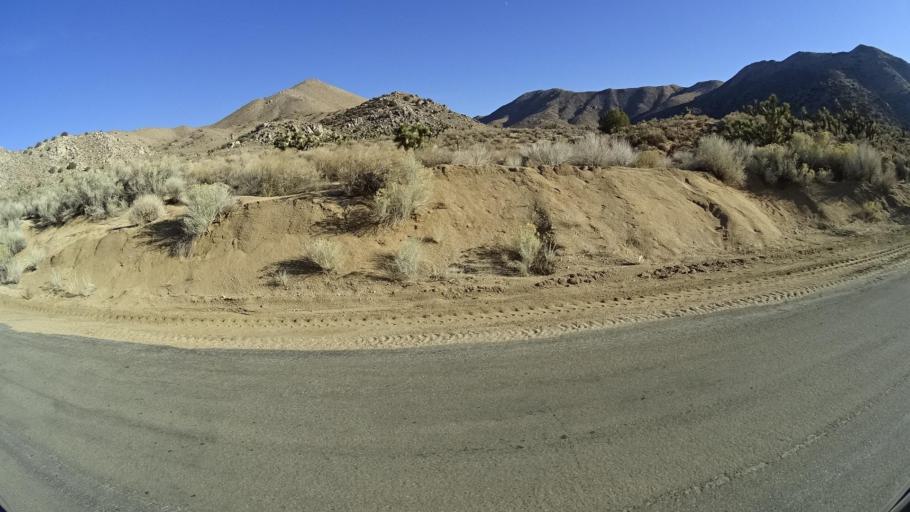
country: US
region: California
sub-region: Kern County
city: Weldon
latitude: 35.5884
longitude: -118.2420
